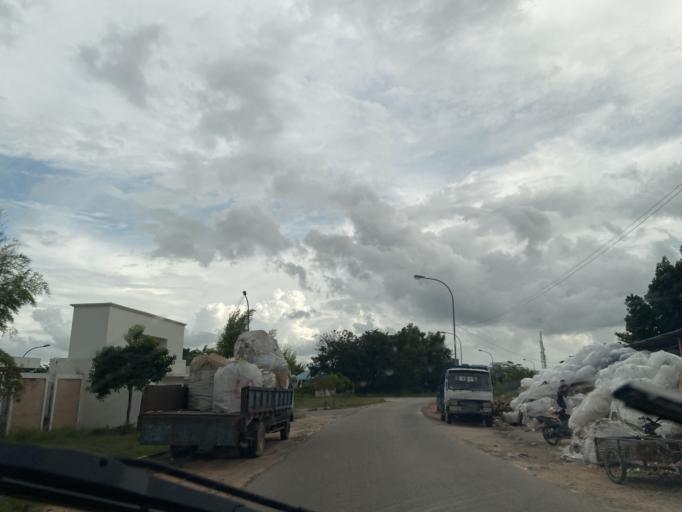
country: SG
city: Singapore
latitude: 1.1175
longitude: 104.0526
